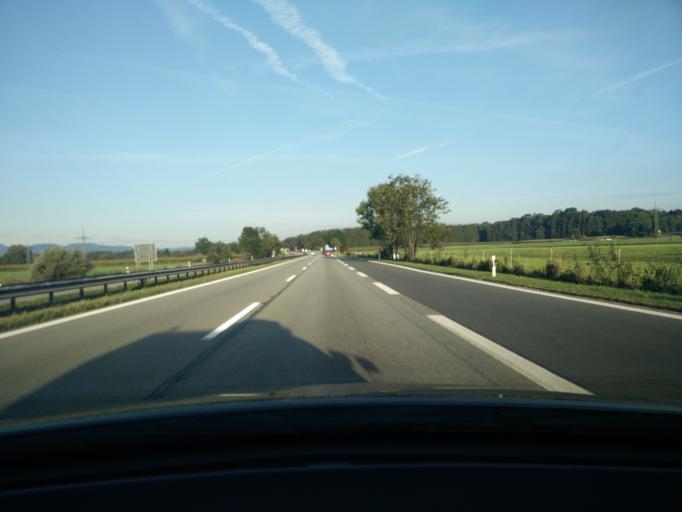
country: DE
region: Bavaria
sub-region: Upper Bavaria
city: Rohrdorf
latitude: 47.8042
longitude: 12.1600
